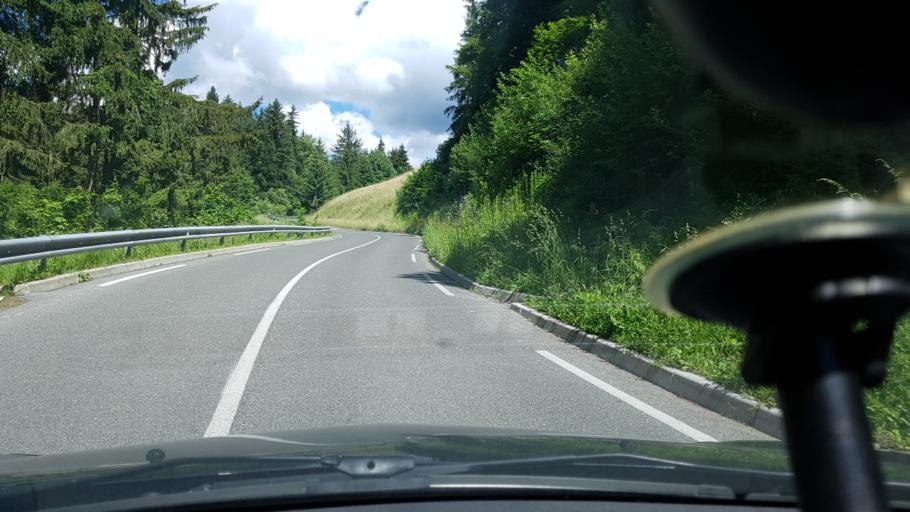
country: SI
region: Zrece
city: Zrece
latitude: 46.3956
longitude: 15.3727
